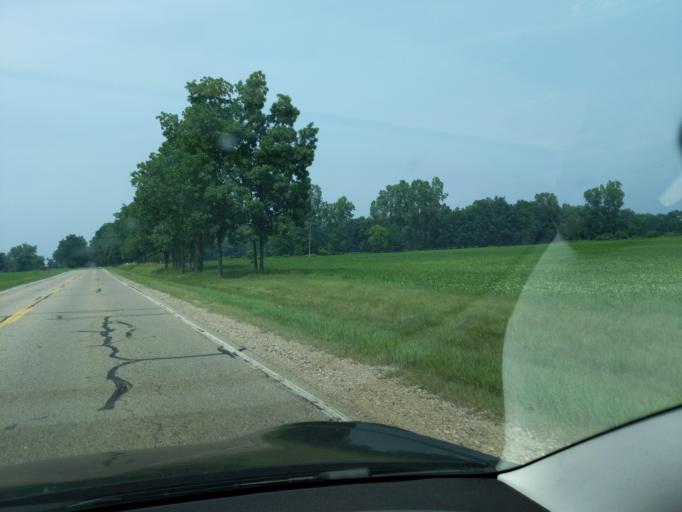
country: US
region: Michigan
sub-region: Ingham County
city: Edgemont Park
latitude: 42.7853
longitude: -84.5694
